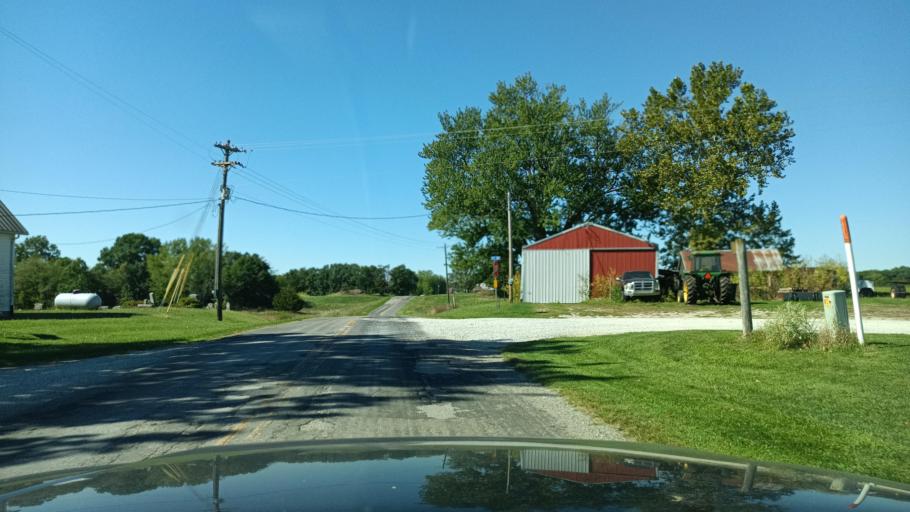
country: US
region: Missouri
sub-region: Scotland County
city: Memphis
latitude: 40.3531
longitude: -92.3028
